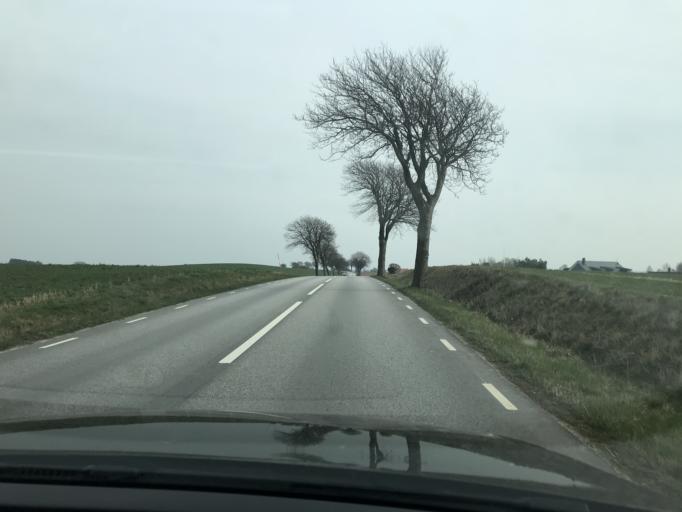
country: SE
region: Skane
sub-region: Skurups Kommun
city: Skivarp
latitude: 55.4212
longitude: 13.6257
